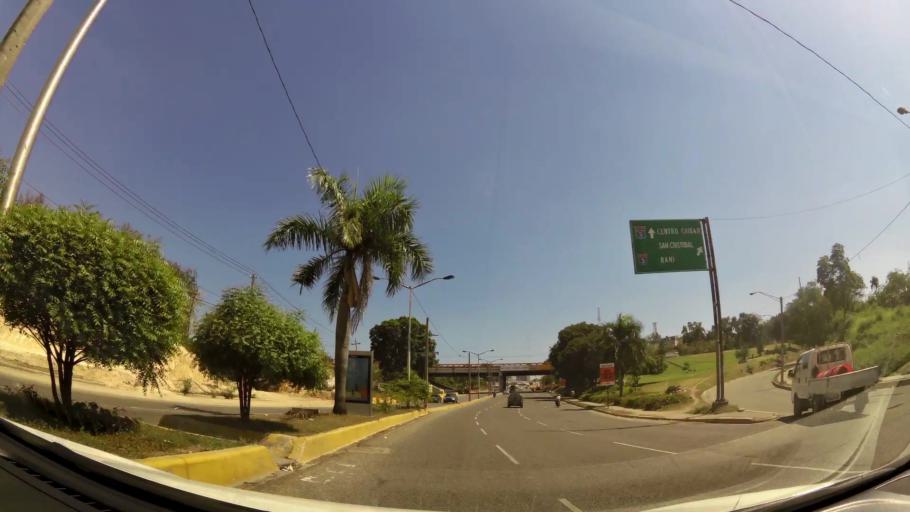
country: DO
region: Nacional
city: Bella Vista
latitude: 18.4560
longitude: -69.9819
